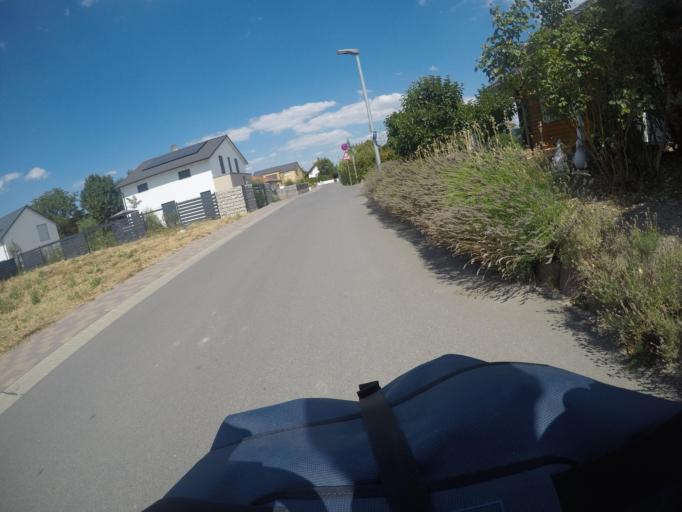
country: DE
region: Rheinland-Pfalz
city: Ludwigshohe
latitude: 49.8158
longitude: 8.3463
